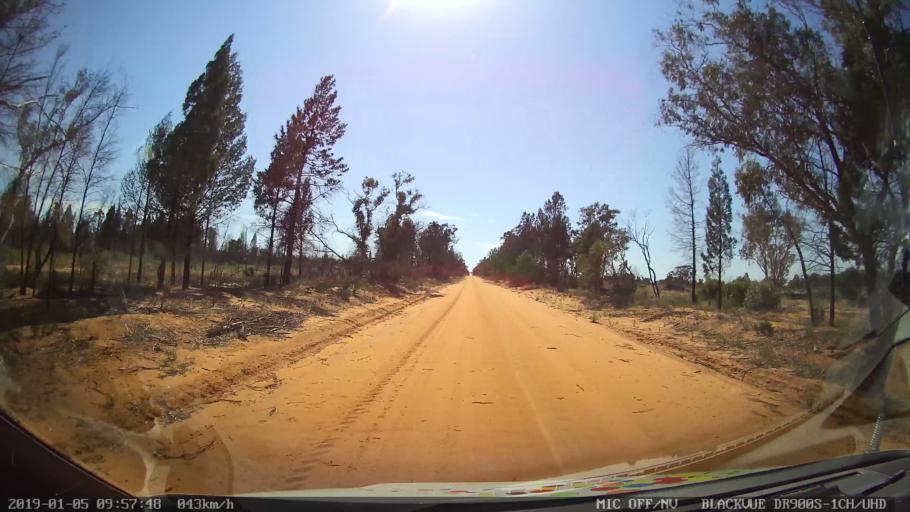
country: AU
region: New South Wales
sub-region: Gilgandra
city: Gilgandra
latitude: -31.6659
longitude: 148.8041
